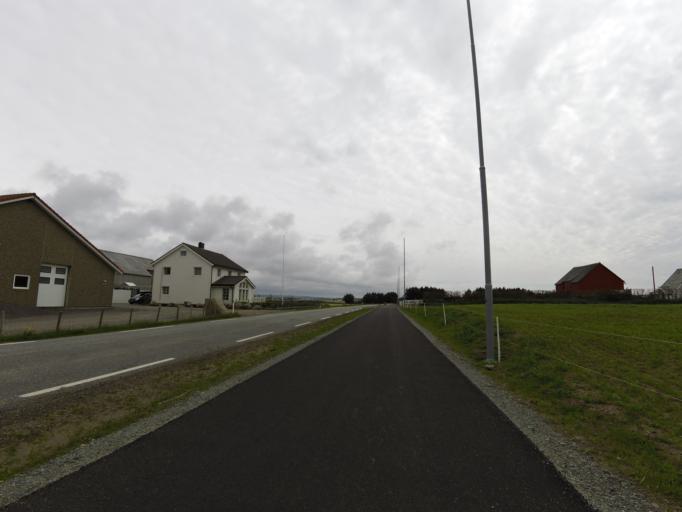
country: NO
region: Rogaland
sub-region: Ha
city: Naerbo
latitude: 58.6931
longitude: 5.5557
